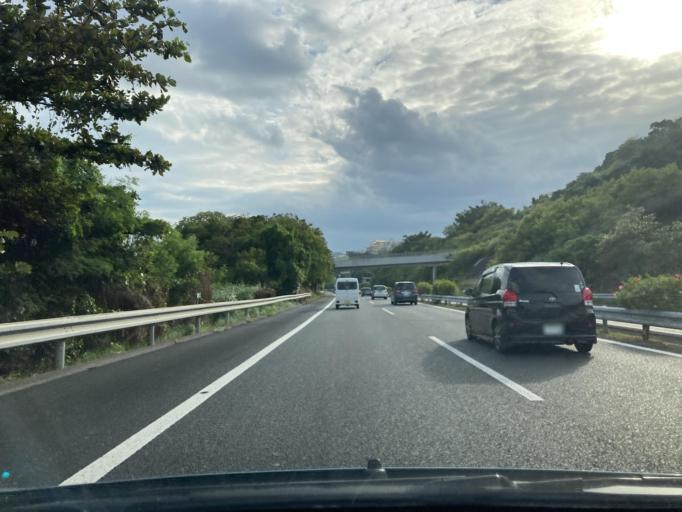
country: JP
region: Okinawa
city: Ginowan
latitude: 26.2726
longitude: 127.7780
